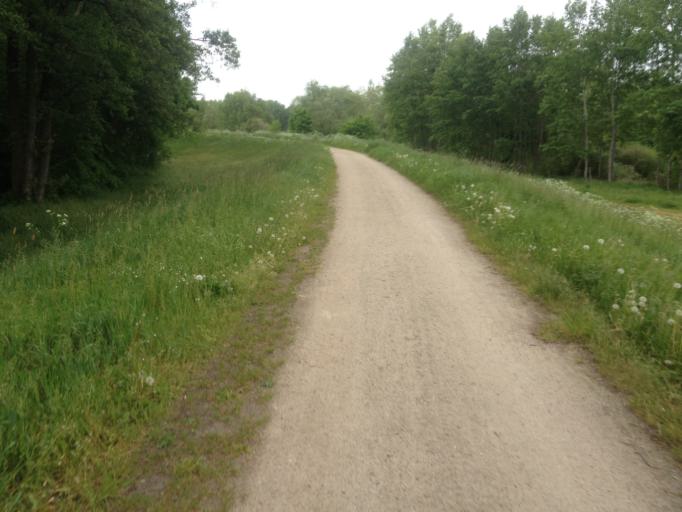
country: DE
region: Brandenburg
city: Drehnow
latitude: 51.8206
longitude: 14.3538
